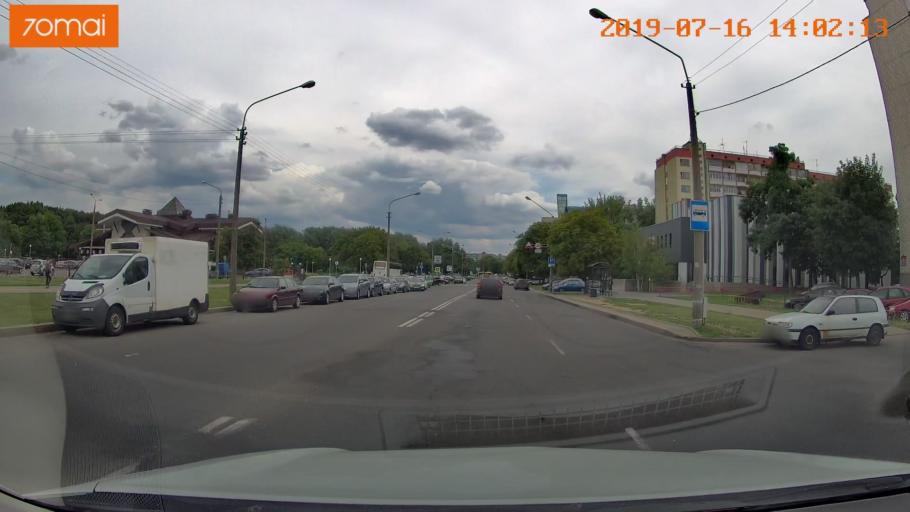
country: BY
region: Minsk
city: Minsk
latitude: 53.9280
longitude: 27.5664
